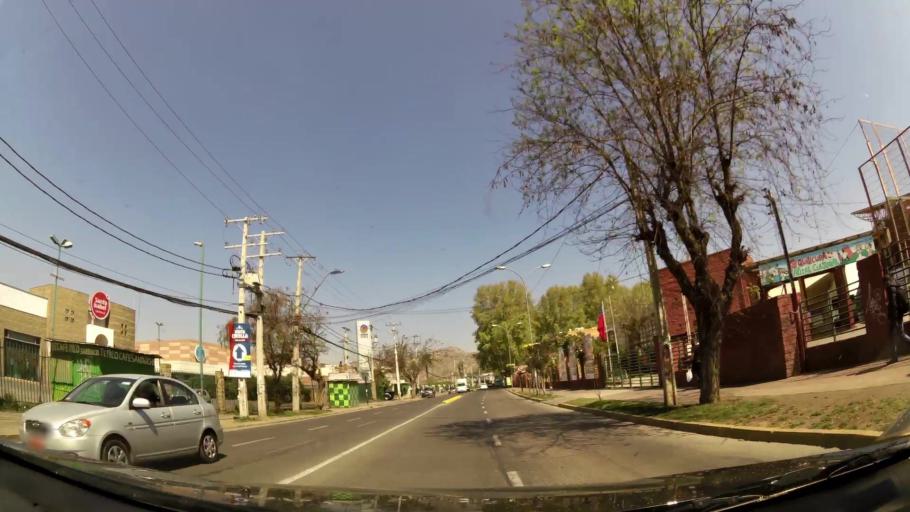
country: CL
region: Santiago Metropolitan
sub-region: Provincia de Santiago
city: Lo Prado
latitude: -33.3666
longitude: -70.7304
